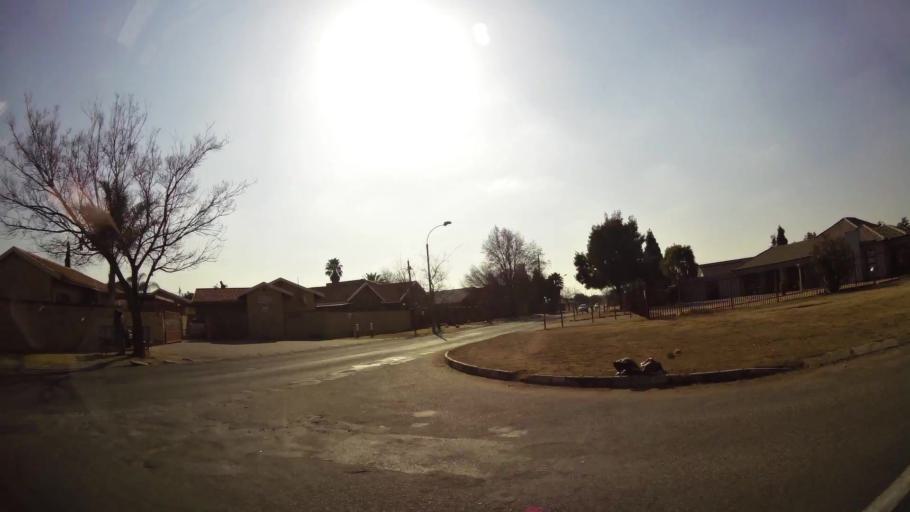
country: ZA
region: Gauteng
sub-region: West Rand District Municipality
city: Randfontein
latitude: -26.1829
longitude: 27.6806
